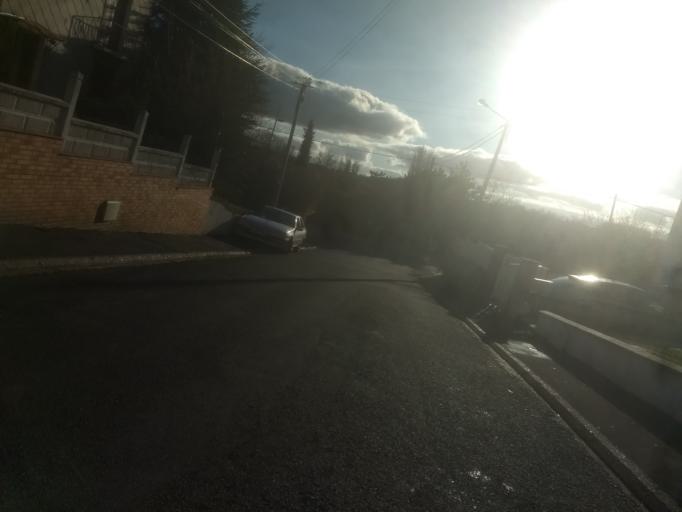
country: FR
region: Nord-Pas-de-Calais
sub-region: Departement du Pas-de-Calais
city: Arras
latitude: 50.3011
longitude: 2.7929
